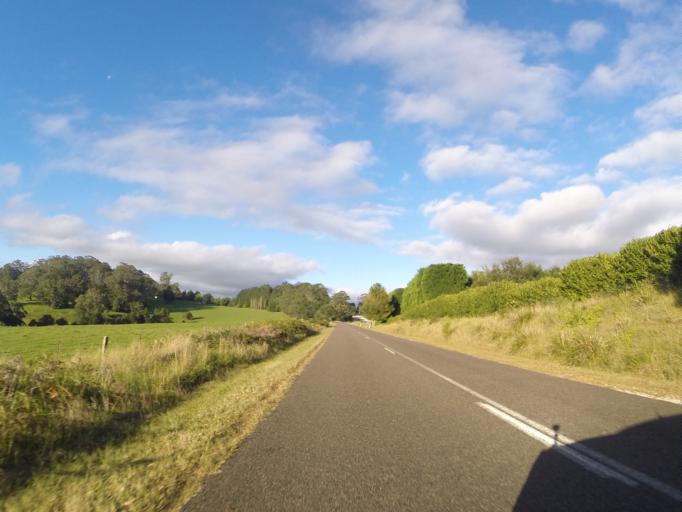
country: AU
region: New South Wales
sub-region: Shoalhaven Shire
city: Kangaroo Valley
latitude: -34.6402
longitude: 150.5168
